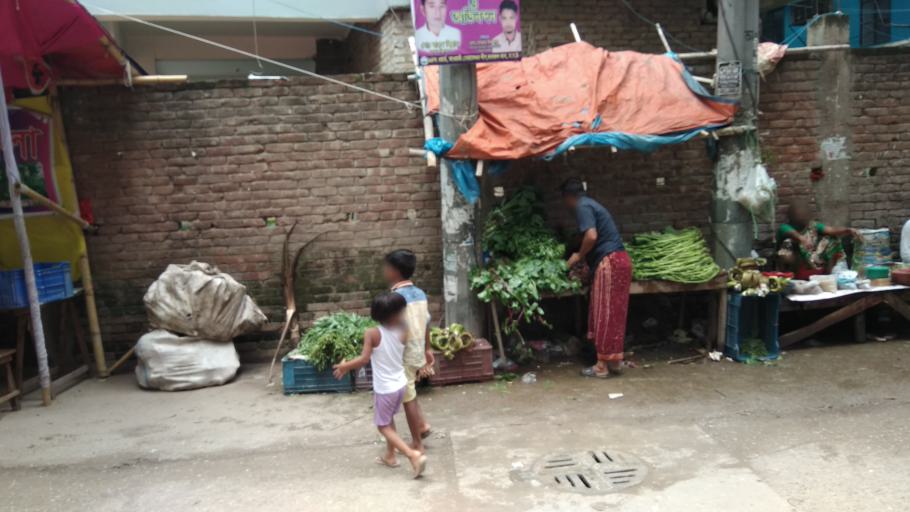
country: BD
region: Dhaka
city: Azimpur
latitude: 23.8035
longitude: 90.3727
